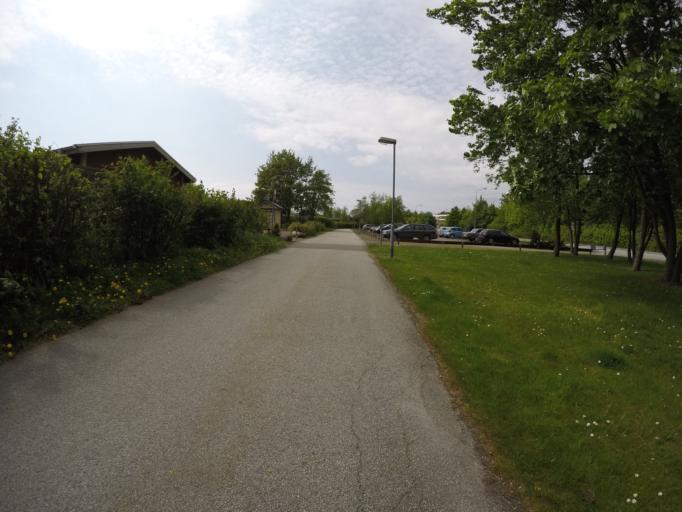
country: SE
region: Skane
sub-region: Malmo
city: Tygelsjo
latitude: 55.5563
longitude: 12.9906
